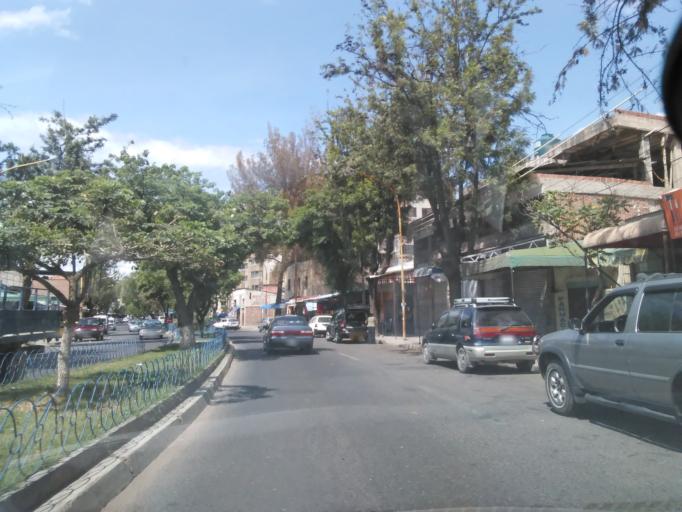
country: BO
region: Cochabamba
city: Cochabamba
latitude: -17.4008
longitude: -66.1628
